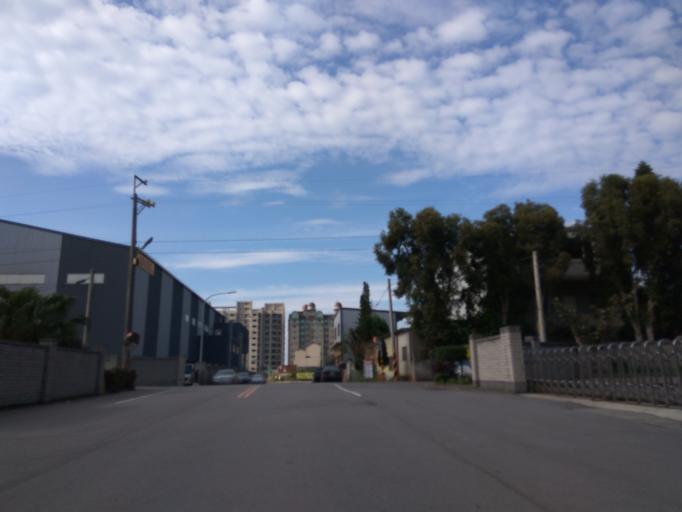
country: TW
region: Taiwan
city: Taoyuan City
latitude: 25.0492
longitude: 121.1769
